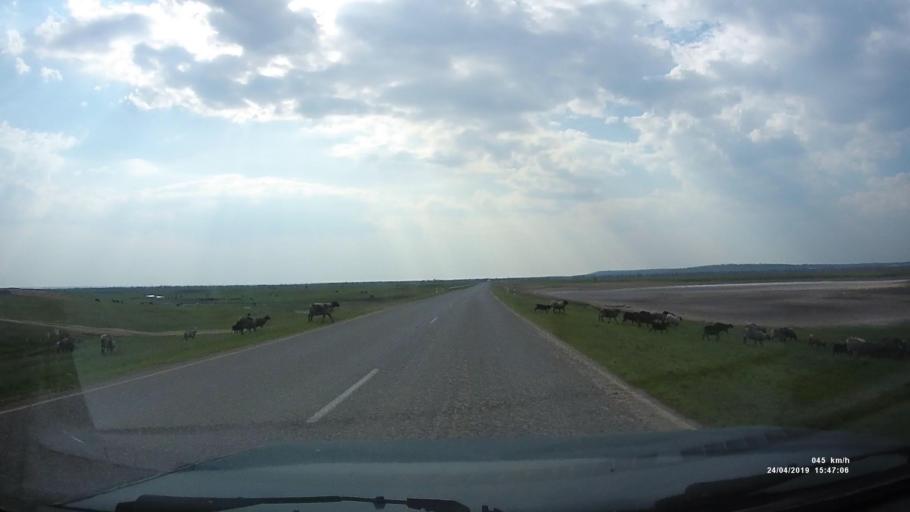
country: RU
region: Kalmykiya
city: Yashalta
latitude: 46.5937
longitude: 42.7017
